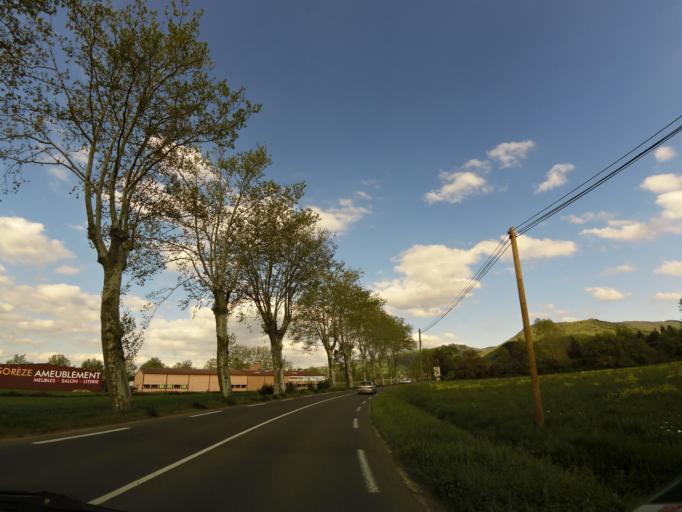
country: FR
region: Midi-Pyrenees
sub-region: Departement du Tarn
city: Soreze
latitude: 43.4520
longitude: 2.0485
